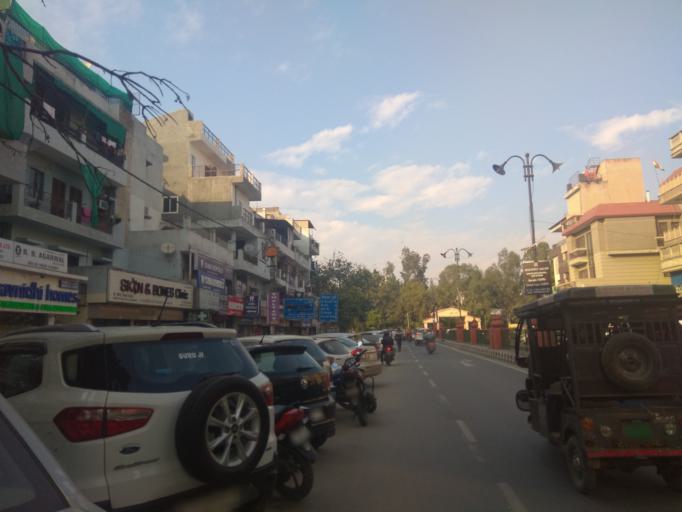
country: IN
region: NCT
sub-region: West Delhi
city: Nangloi Jat
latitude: 28.6346
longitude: 77.0689
